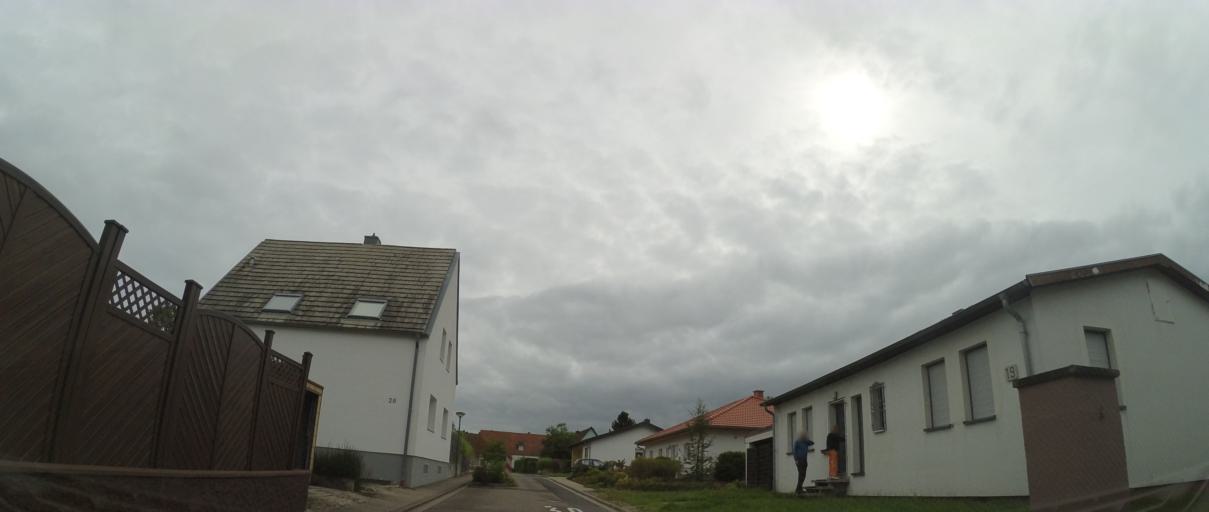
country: DE
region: Saarland
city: Bexbach
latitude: 49.3277
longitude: 7.2888
